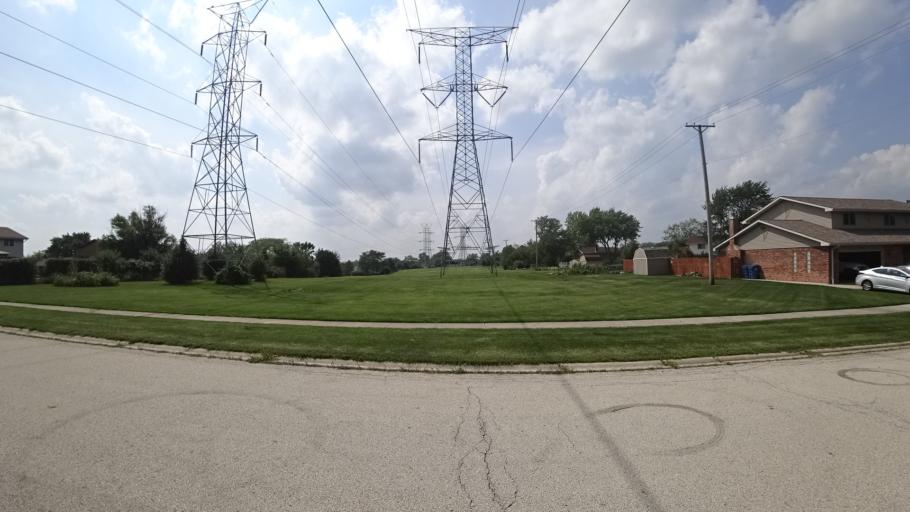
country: US
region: Illinois
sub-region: Will County
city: Goodings Grove
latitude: 41.6407
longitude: -87.9076
